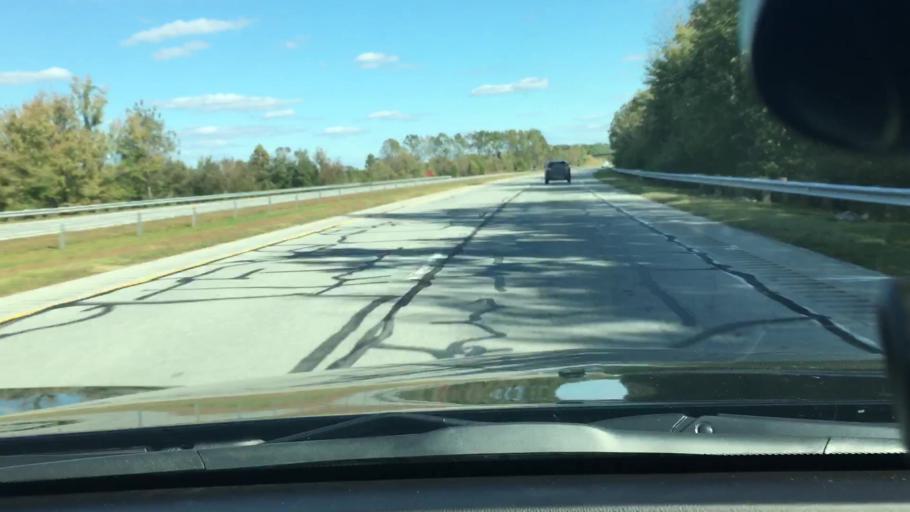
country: US
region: North Carolina
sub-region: Pitt County
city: Farmville
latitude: 35.6166
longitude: -77.6495
